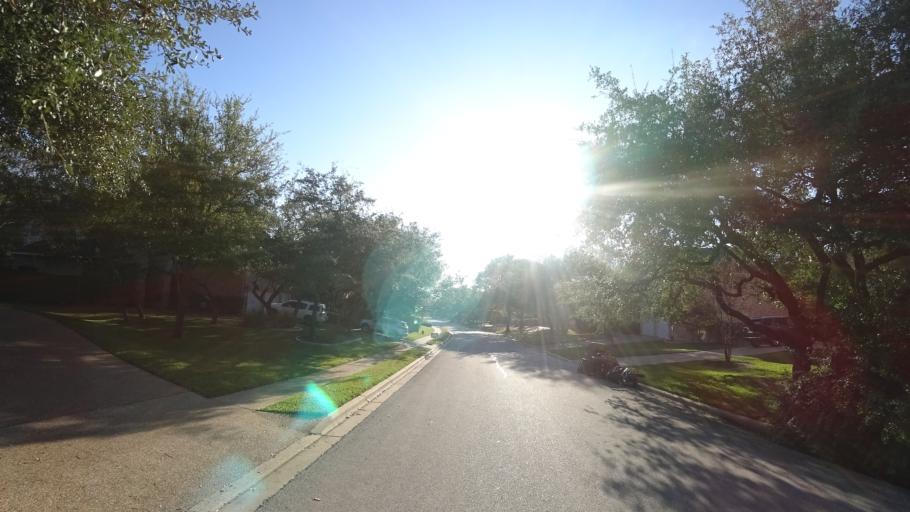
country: US
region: Texas
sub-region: Travis County
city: Hudson Bend
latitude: 30.3735
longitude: -97.8824
